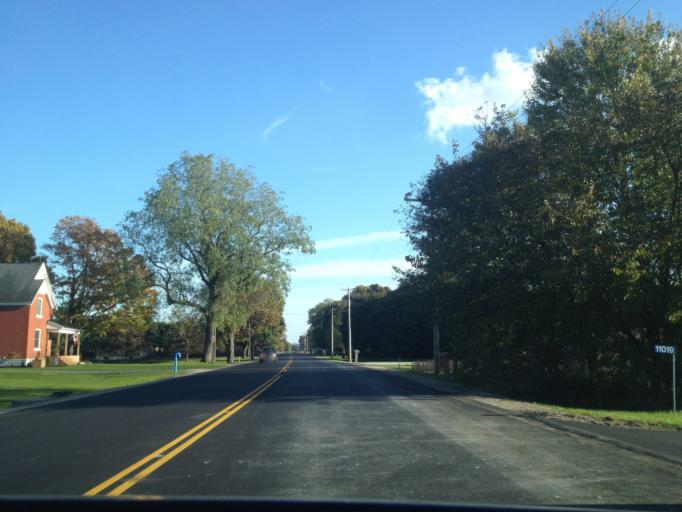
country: CA
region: Ontario
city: Delaware
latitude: 42.5946
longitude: -81.5954
